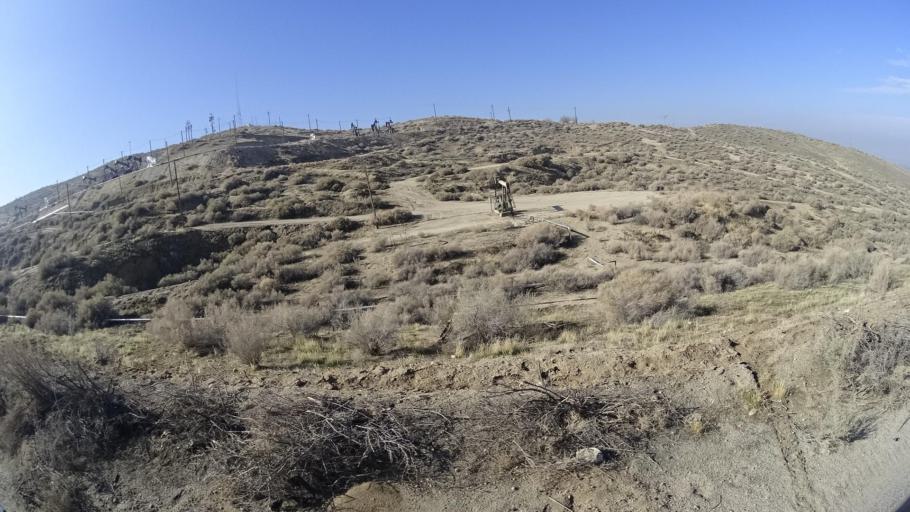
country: US
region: California
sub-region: Kern County
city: South Taft
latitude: 35.1190
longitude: -119.4563
